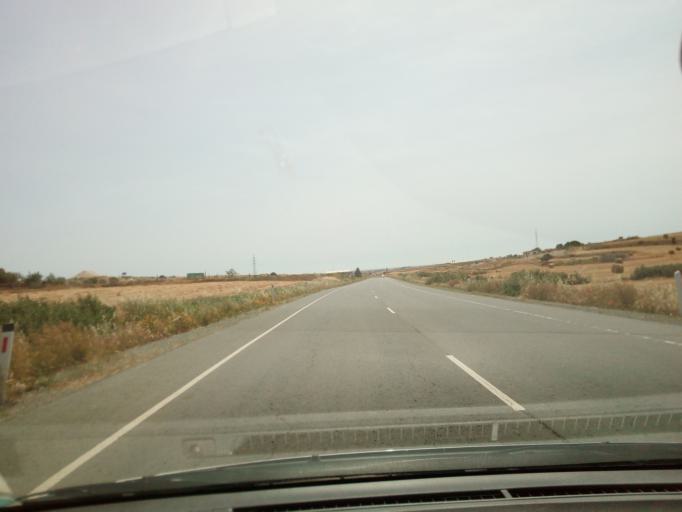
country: CY
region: Larnaka
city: Aradippou
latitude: 34.9822
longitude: 33.5790
